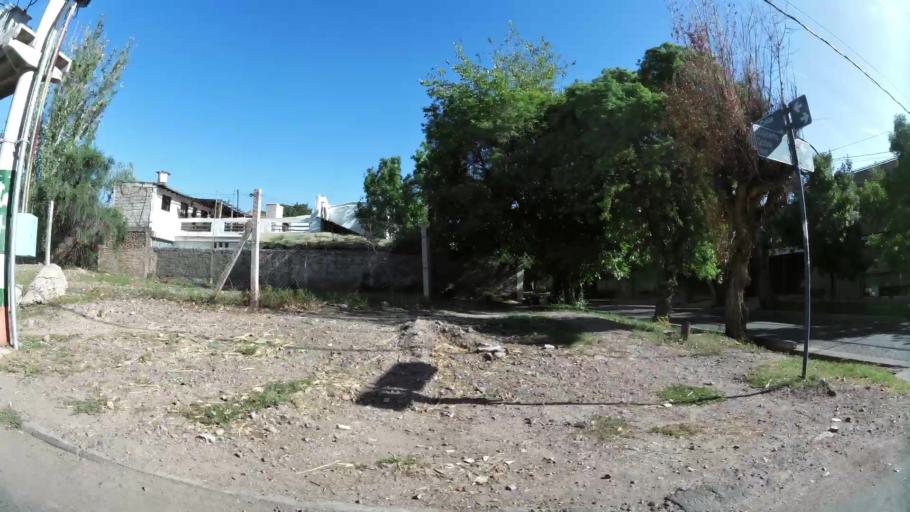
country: AR
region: Mendoza
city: Mendoza
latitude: -32.9025
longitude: -68.8174
